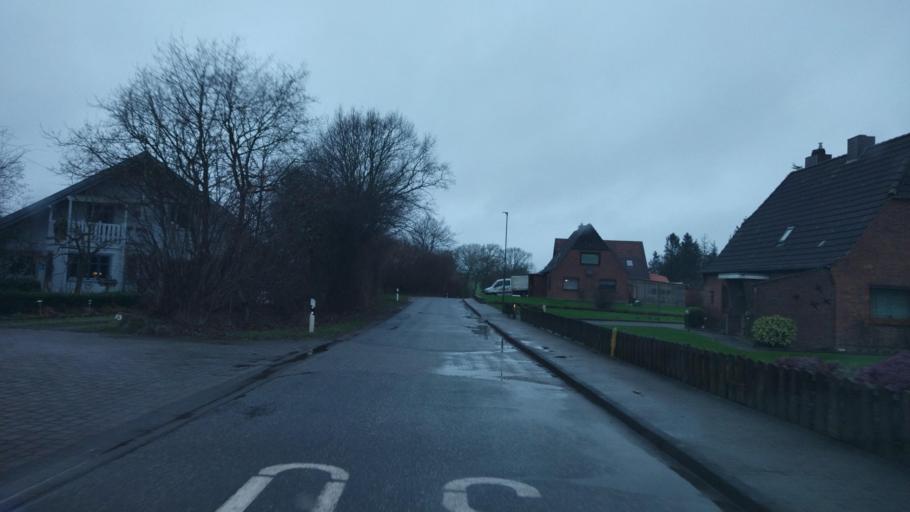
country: DE
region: Schleswig-Holstein
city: Guby
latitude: 54.4867
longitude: 9.6642
